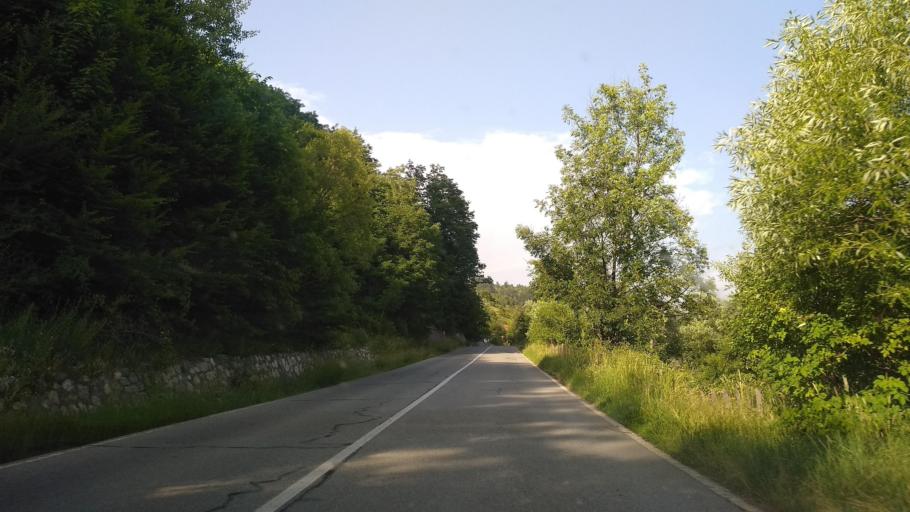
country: RO
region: Hunedoara
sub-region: Comuna Uricani
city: Uricani
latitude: 45.3222
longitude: 23.0889
